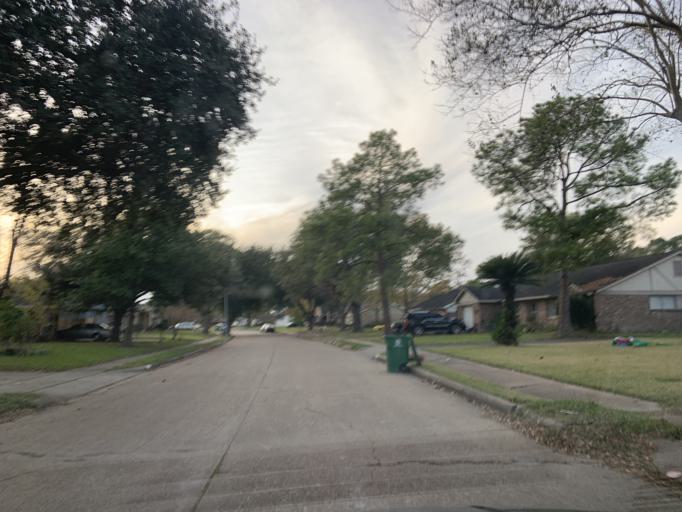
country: US
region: Texas
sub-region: Harris County
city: Bellaire
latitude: 29.6948
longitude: -95.5078
